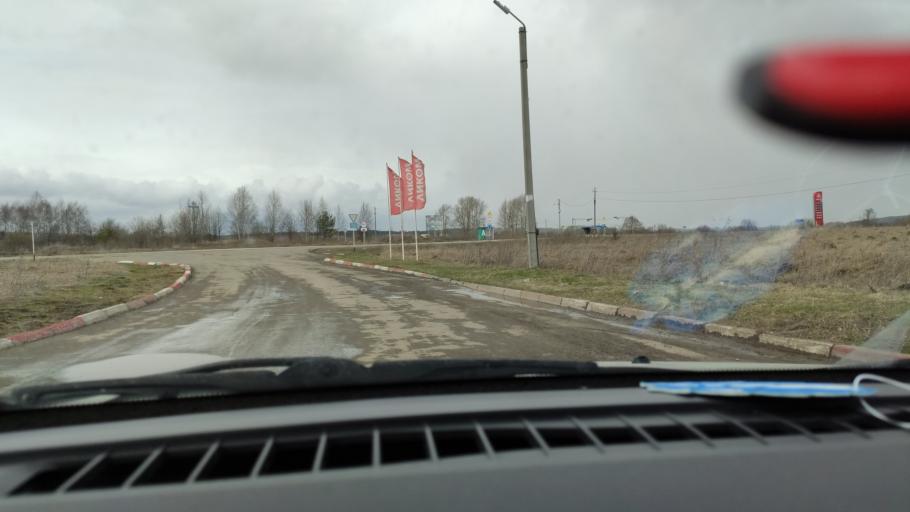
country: RU
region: Perm
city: Kukushtan
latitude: 57.5026
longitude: 56.6503
